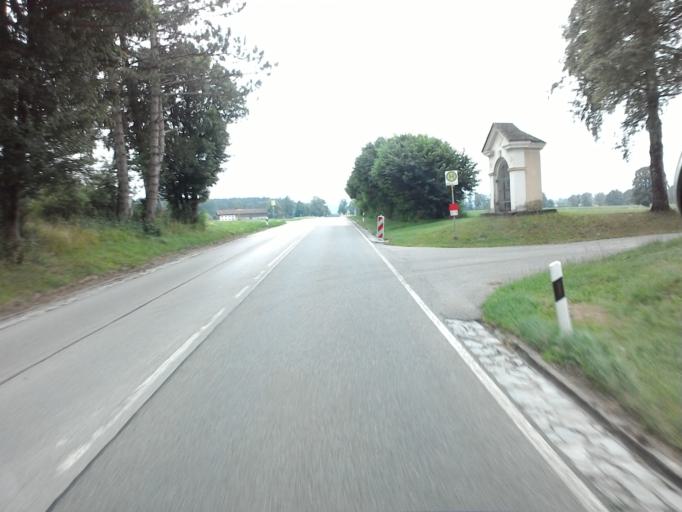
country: DE
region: Bavaria
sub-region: Upper Bavaria
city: Miesbach
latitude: 47.8082
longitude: 11.8383
